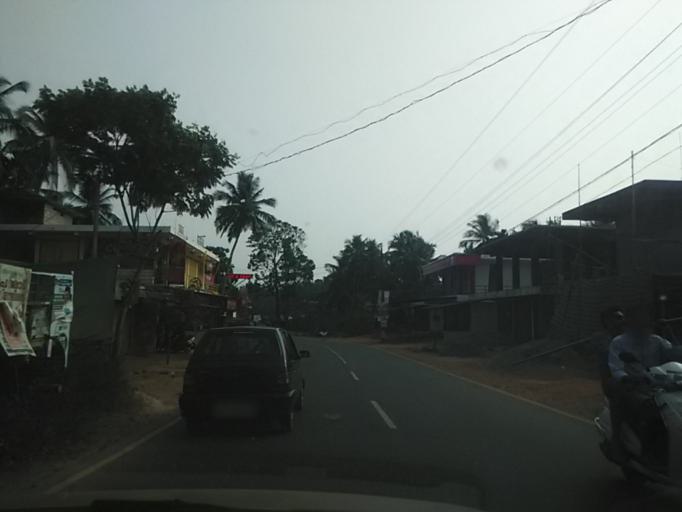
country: IN
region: Kerala
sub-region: Kozhikode
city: Naduvannur
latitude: 11.4902
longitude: 75.7751
